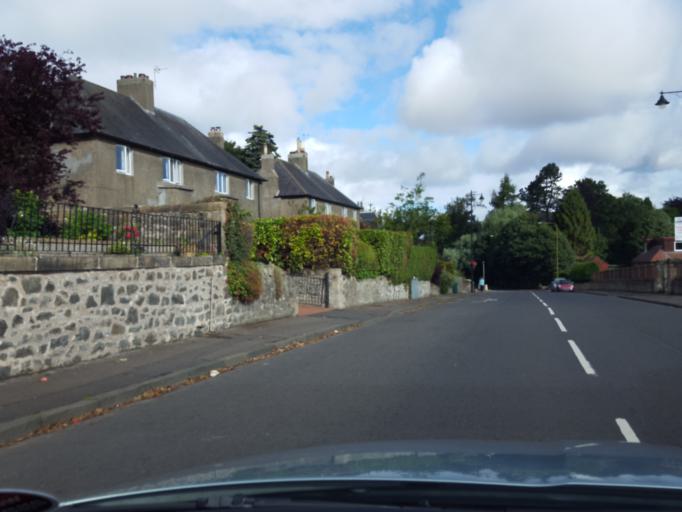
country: GB
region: Scotland
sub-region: West Lothian
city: Linlithgow
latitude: 55.9780
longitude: -3.6111
